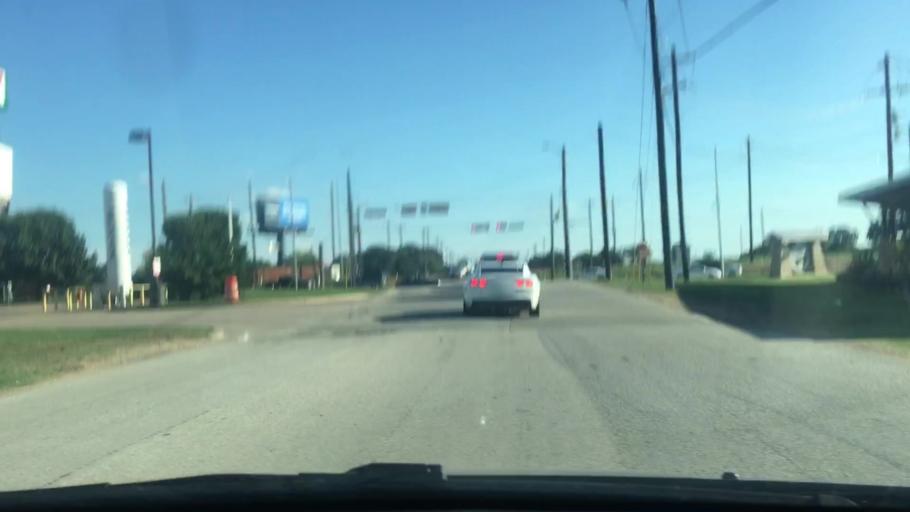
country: US
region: Texas
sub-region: Denton County
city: Cross Roads
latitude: 33.2248
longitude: -96.9764
